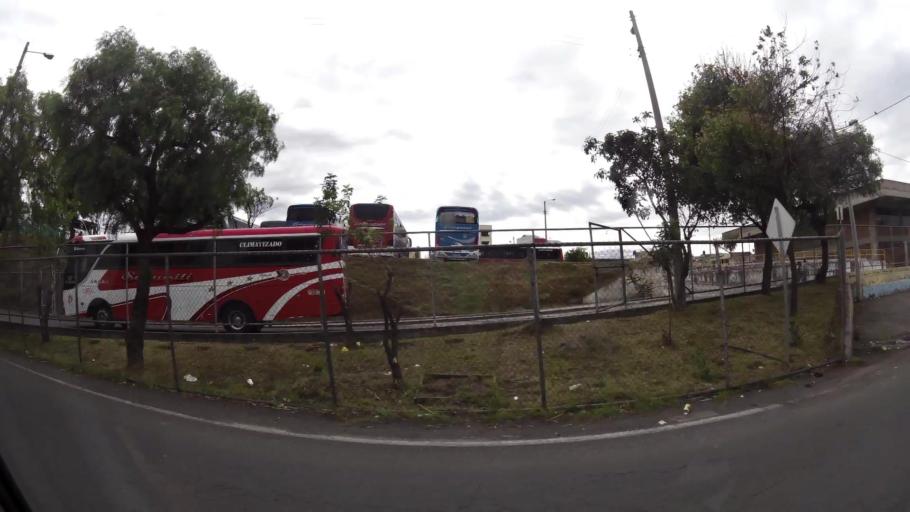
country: EC
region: Cotopaxi
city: Latacunga
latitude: -0.9352
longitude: -78.6203
